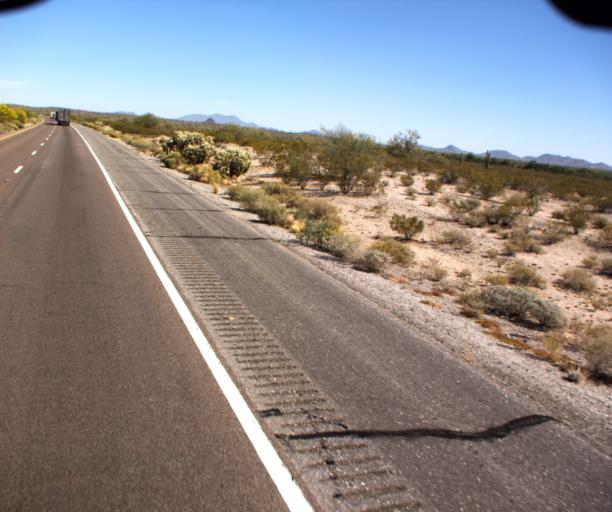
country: US
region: Arizona
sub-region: Maricopa County
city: Gila Bend
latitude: 32.8514
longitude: -112.3605
